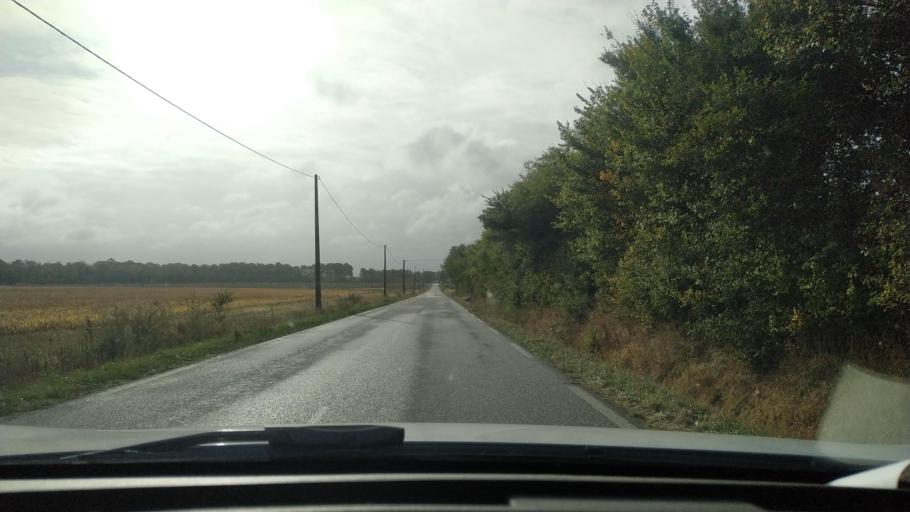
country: FR
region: Midi-Pyrenees
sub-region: Departement de la Haute-Garonne
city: Gaillac-Toulza
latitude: 43.2885
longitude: 1.4837
